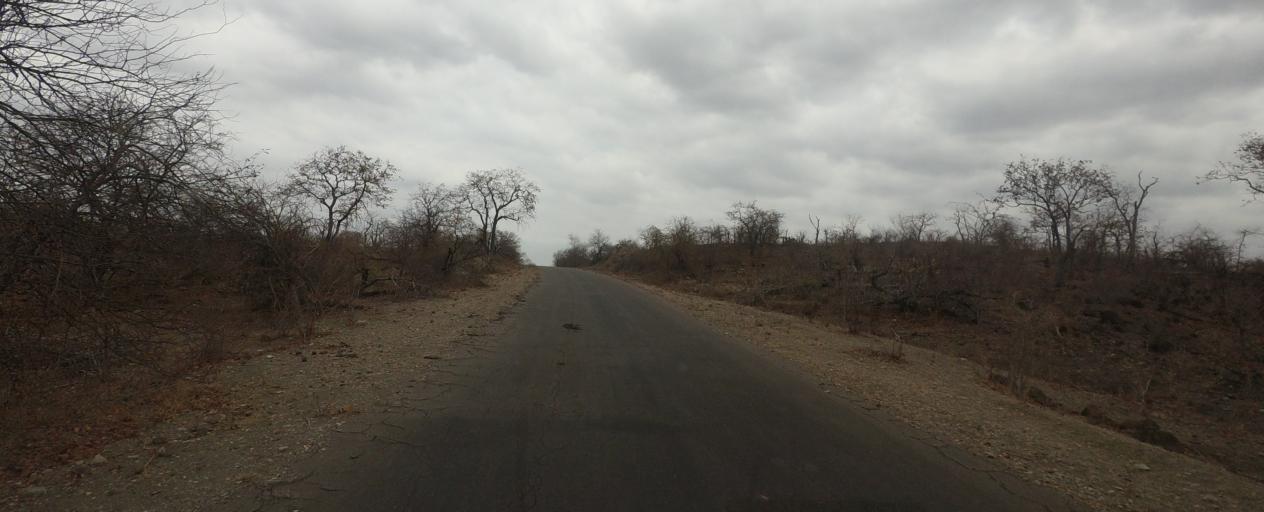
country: ZA
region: Limpopo
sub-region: Vhembe District Municipality
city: Mutale
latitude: -22.4025
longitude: 31.2040
